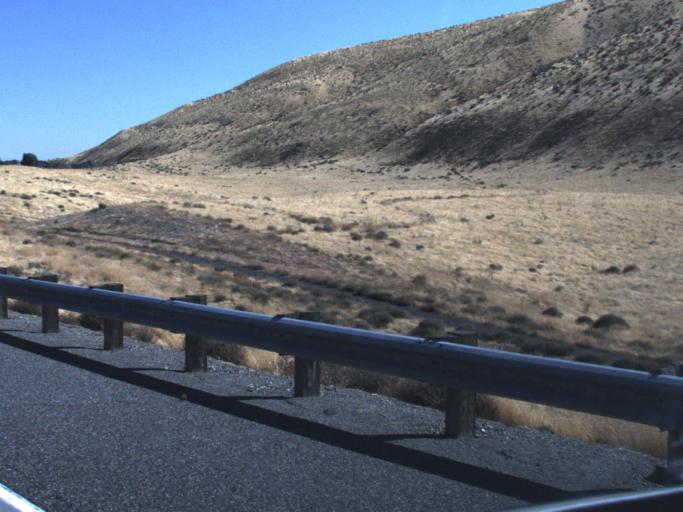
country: US
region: Washington
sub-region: Benton County
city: West Richland
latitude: 46.2465
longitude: -119.3360
